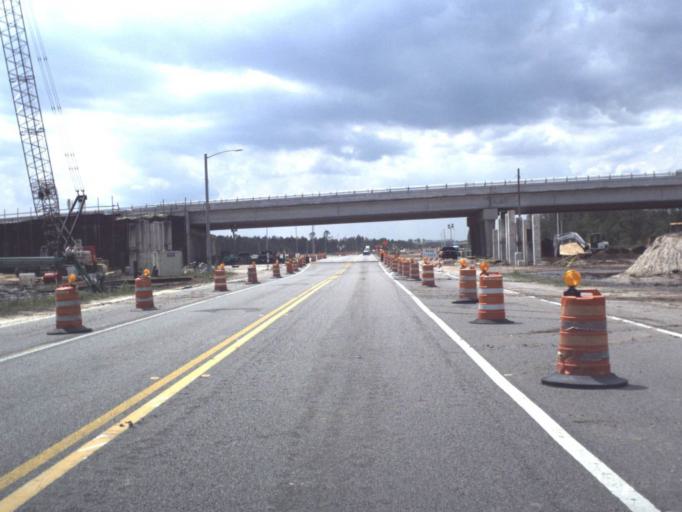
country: US
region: Florida
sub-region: Duval County
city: Baldwin
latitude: 30.2603
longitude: -81.8614
